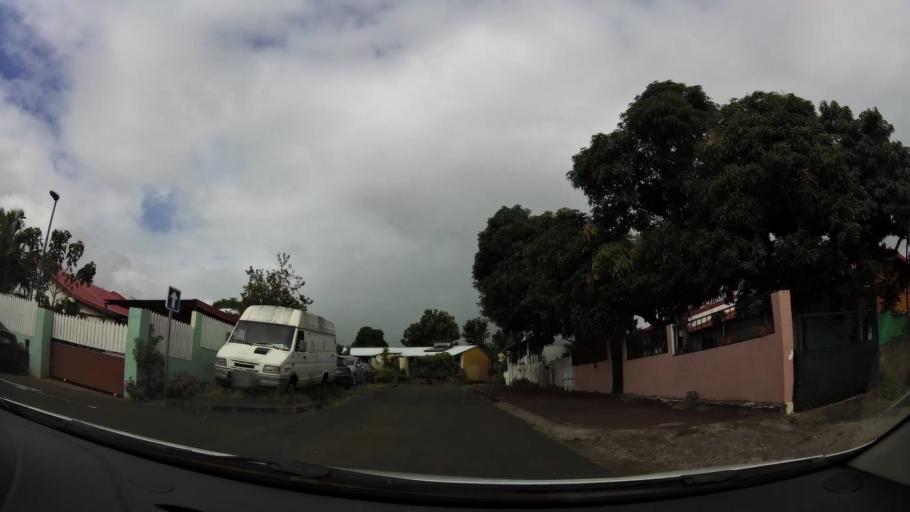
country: RE
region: Reunion
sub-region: Reunion
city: Sainte-Marie
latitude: -20.9006
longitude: 55.5556
